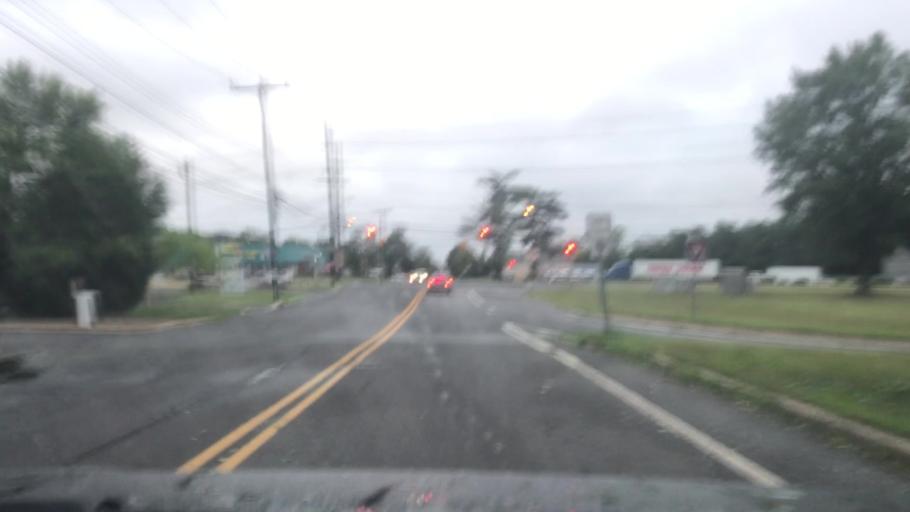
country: US
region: New Jersey
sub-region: Ocean County
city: Toms River
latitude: 39.9596
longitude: -74.1772
